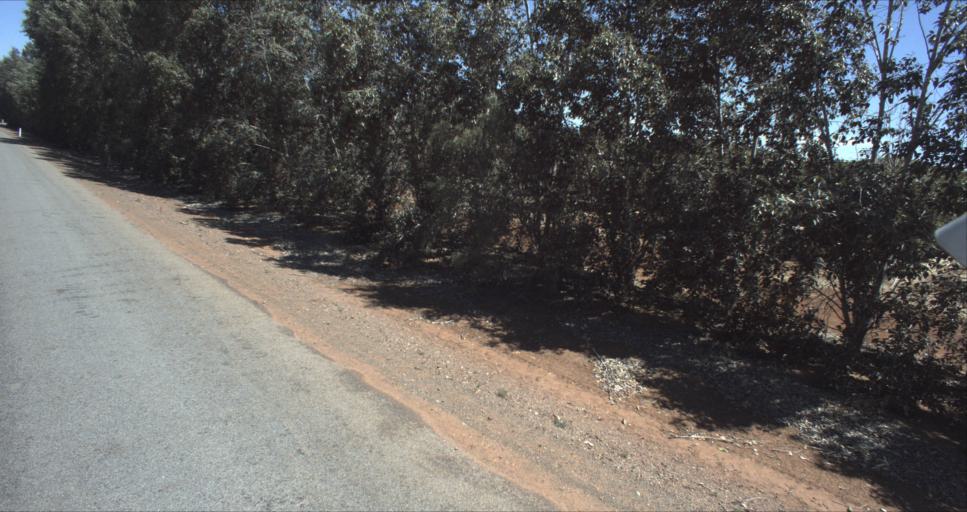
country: AU
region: New South Wales
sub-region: Leeton
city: Leeton
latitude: -34.5268
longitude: 146.3298
